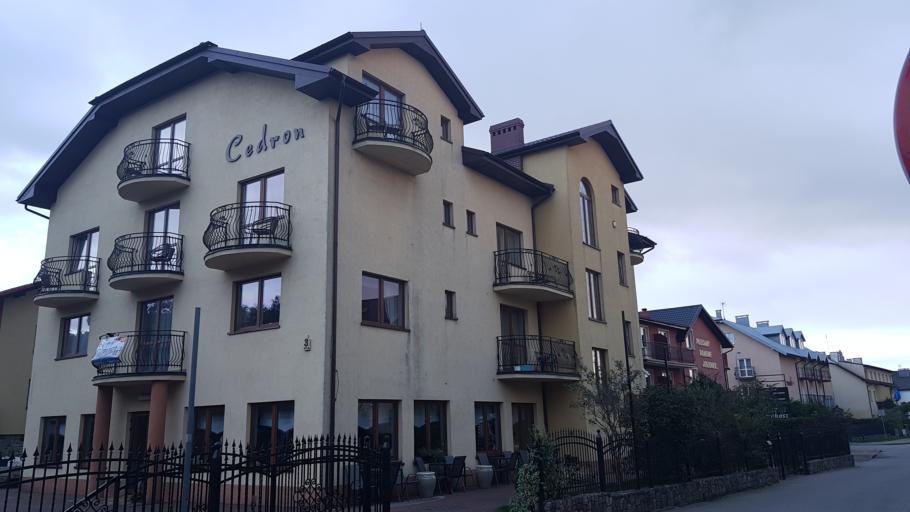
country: PL
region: Pomeranian Voivodeship
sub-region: Powiat pucki
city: Krokowa
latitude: 54.8304
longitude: 18.2147
